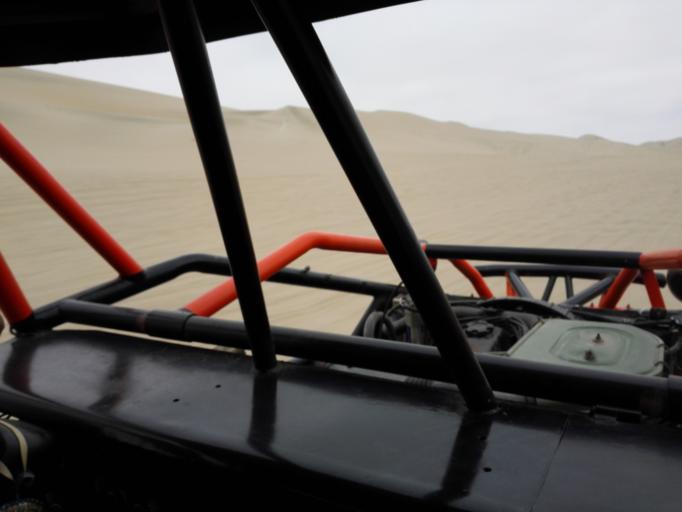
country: PE
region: Ica
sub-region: Provincia de Ica
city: Ica
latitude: -14.0873
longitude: -75.7704
